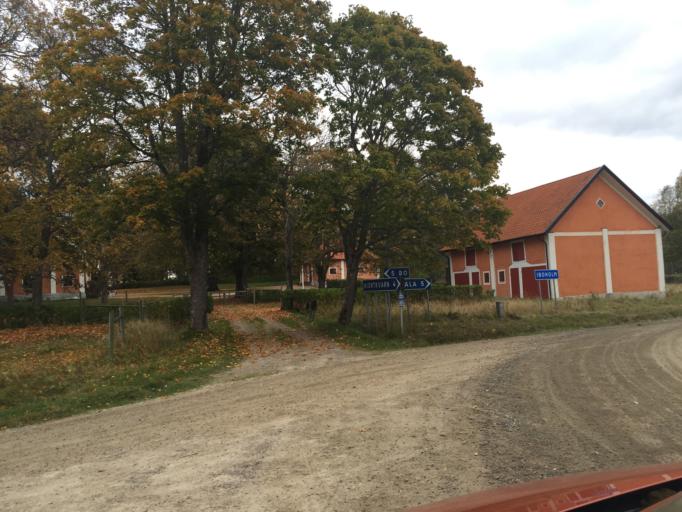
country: SE
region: OErebro
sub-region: Hallsbergs Kommun
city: Palsboda
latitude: 58.8957
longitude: 15.4937
